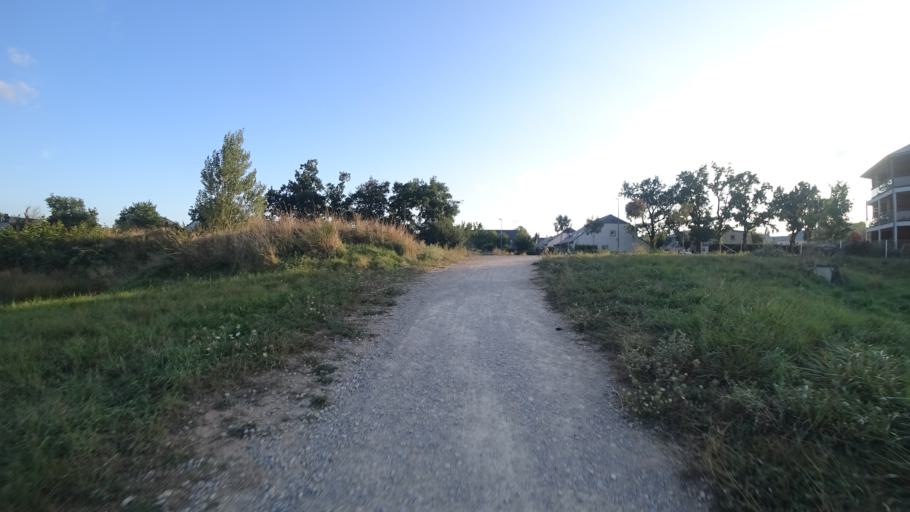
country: FR
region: Midi-Pyrenees
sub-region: Departement de l'Aveyron
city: Rodez
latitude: 44.3765
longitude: 2.5828
